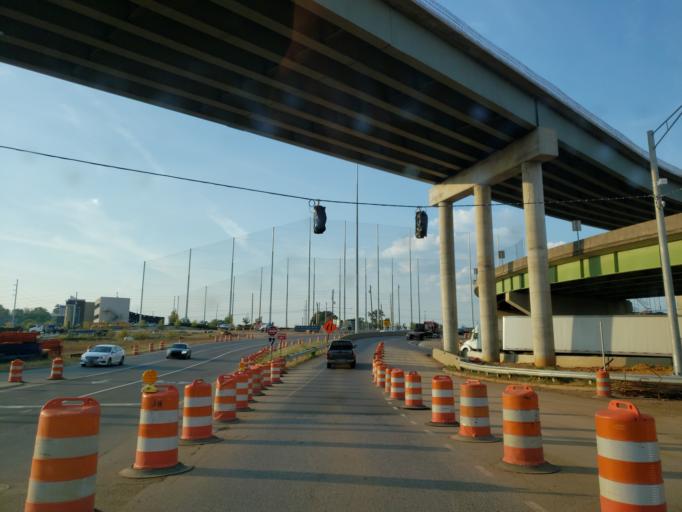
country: US
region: Alabama
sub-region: Jefferson County
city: Birmingham
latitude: 33.5276
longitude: -86.8055
